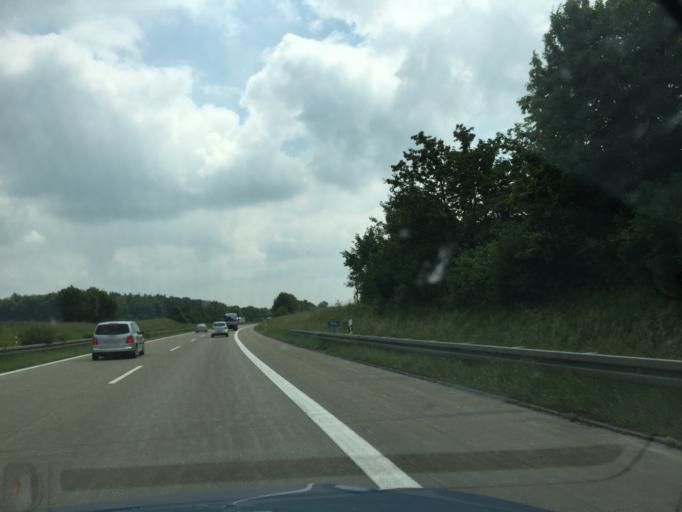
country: DE
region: Baden-Wuerttemberg
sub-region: Regierungsbezirk Stuttgart
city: Lauchheim
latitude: 48.8283
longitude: 10.2137
